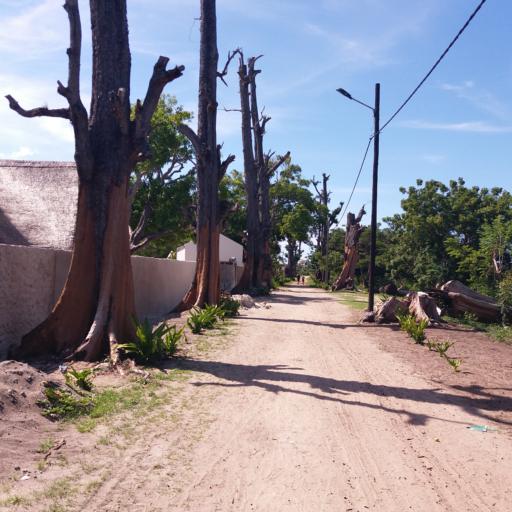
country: MZ
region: Cabo Delgado
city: Pemba
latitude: -12.3409
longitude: 40.5825
